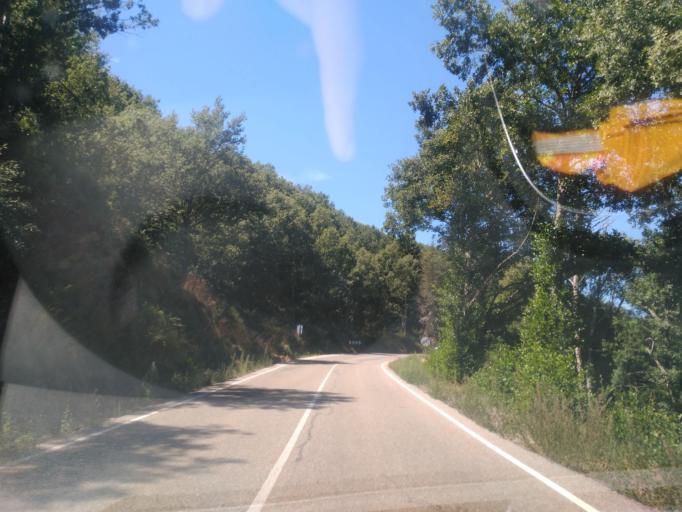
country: ES
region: Castille and Leon
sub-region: Provincia de Zamora
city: Galende
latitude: 42.1071
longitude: -6.6690
